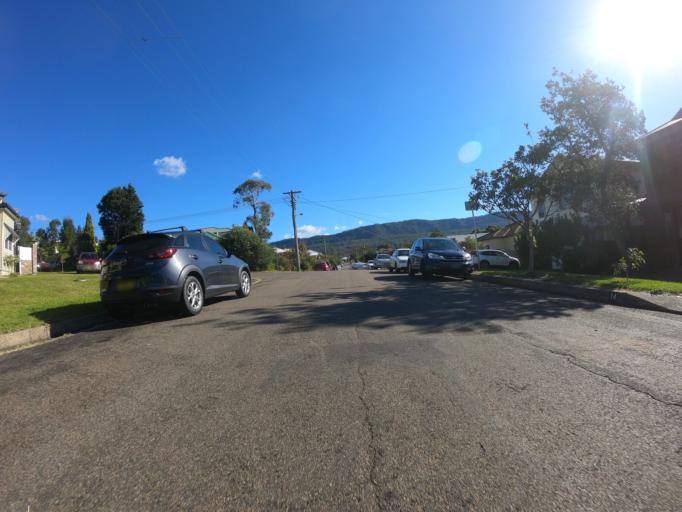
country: AU
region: New South Wales
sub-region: Wollongong
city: Bulli
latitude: -34.3385
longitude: 150.9193
